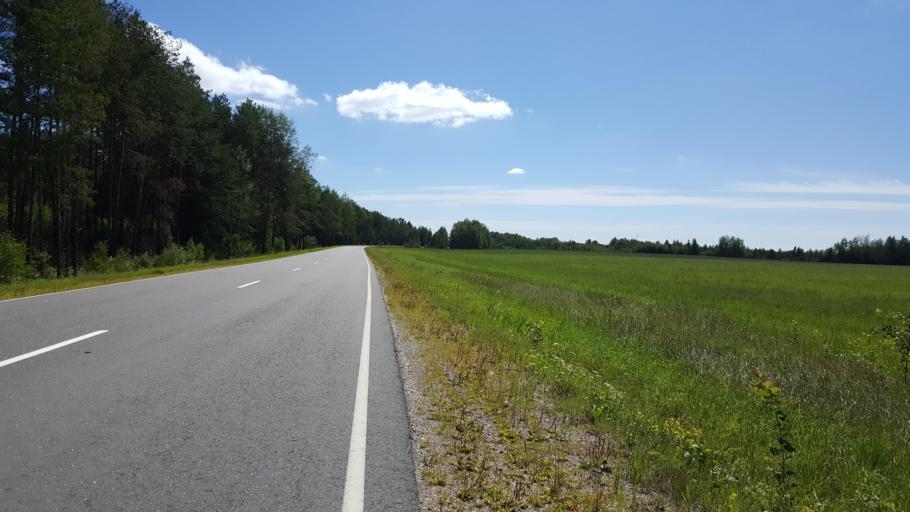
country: BY
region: Brest
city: Zhabinka
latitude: 52.3752
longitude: 24.1310
